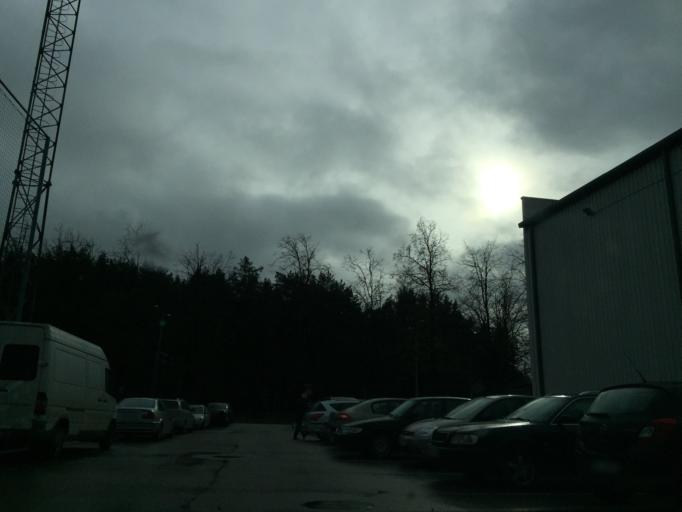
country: LV
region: Riga
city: Jaunciems
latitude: 56.9863
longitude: 24.2092
